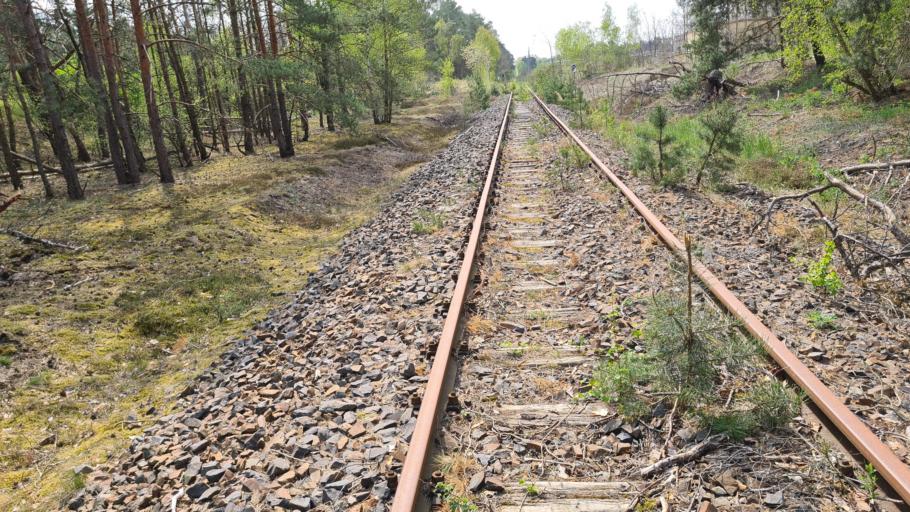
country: DE
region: Brandenburg
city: Finsterwalde
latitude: 51.6556
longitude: 13.6999
